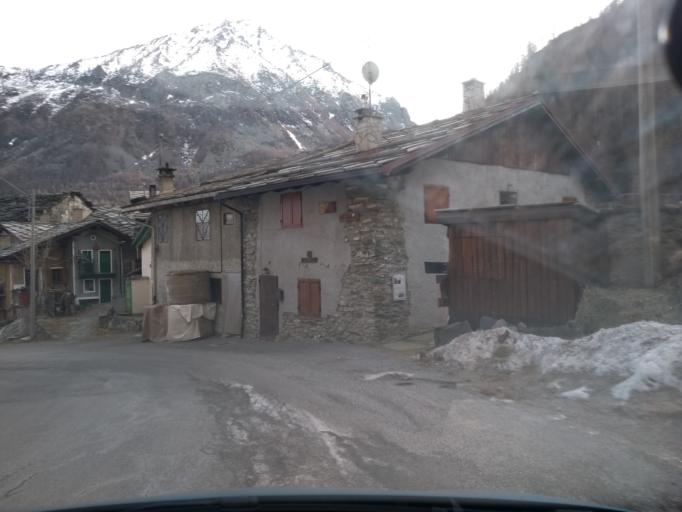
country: IT
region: Piedmont
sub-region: Provincia di Torino
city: Balme
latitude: 45.3024
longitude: 7.2147
